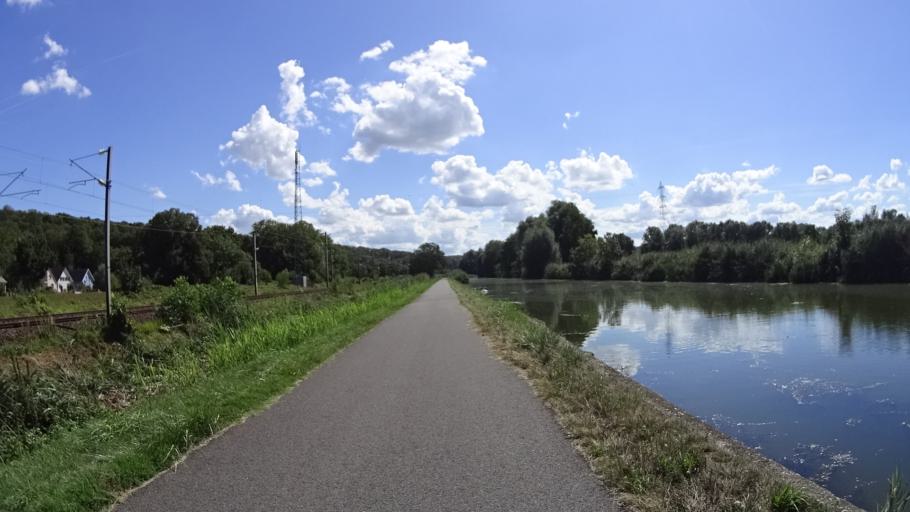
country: FR
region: Alsace
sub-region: Departement du Haut-Rhin
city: Didenheim
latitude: 47.7094
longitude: 7.3112
